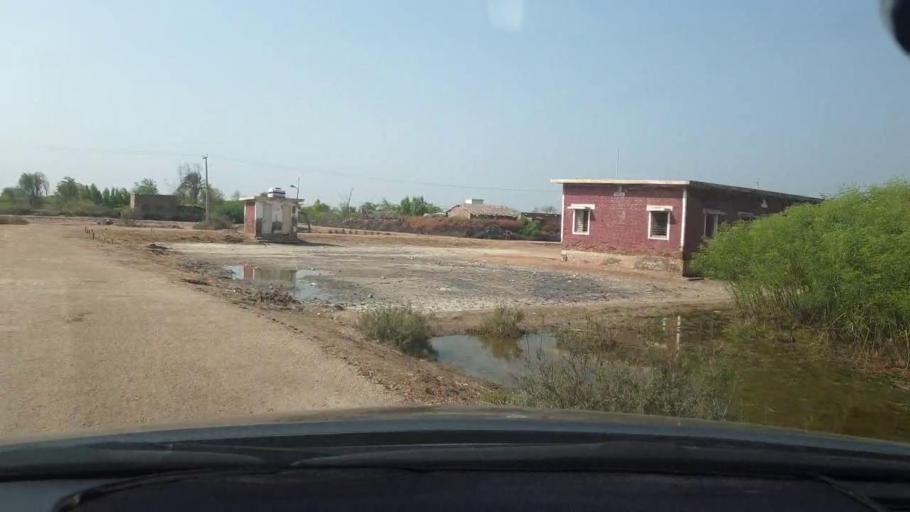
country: PK
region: Sindh
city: Tando Bago
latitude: 24.6889
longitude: 69.1234
